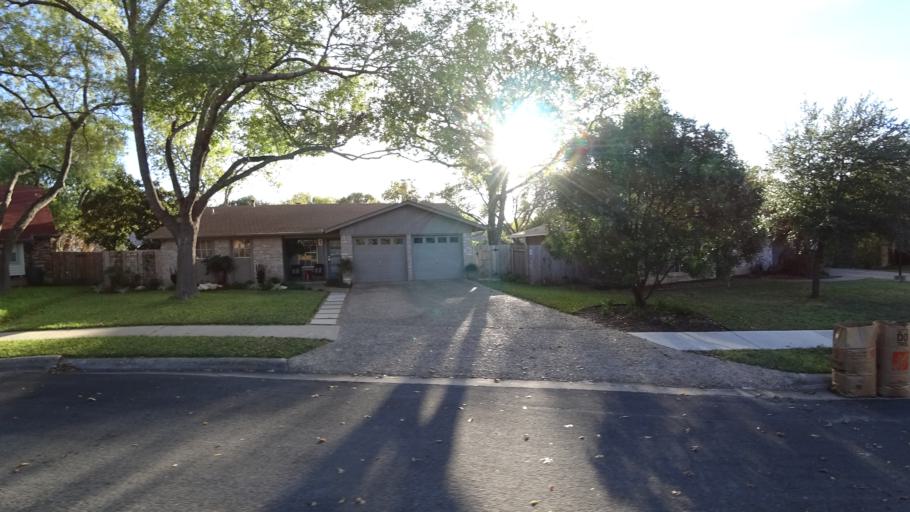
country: US
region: Texas
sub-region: Williamson County
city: Jollyville
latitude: 30.3722
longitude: -97.7350
